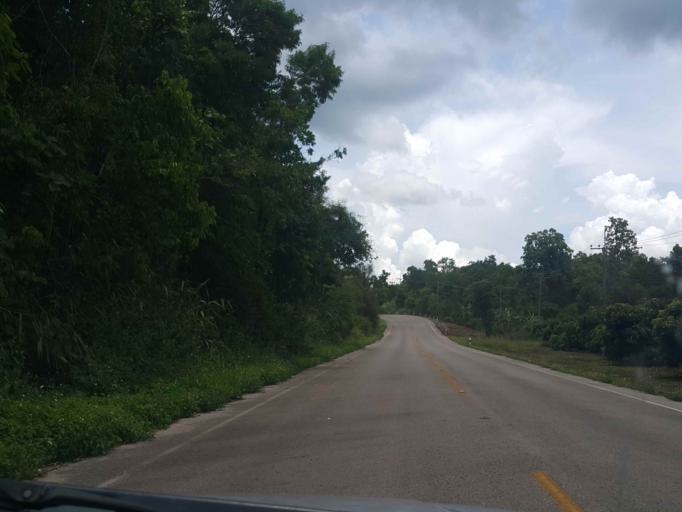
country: TH
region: Phayao
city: Chiang Muan
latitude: 18.9184
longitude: 100.1103
